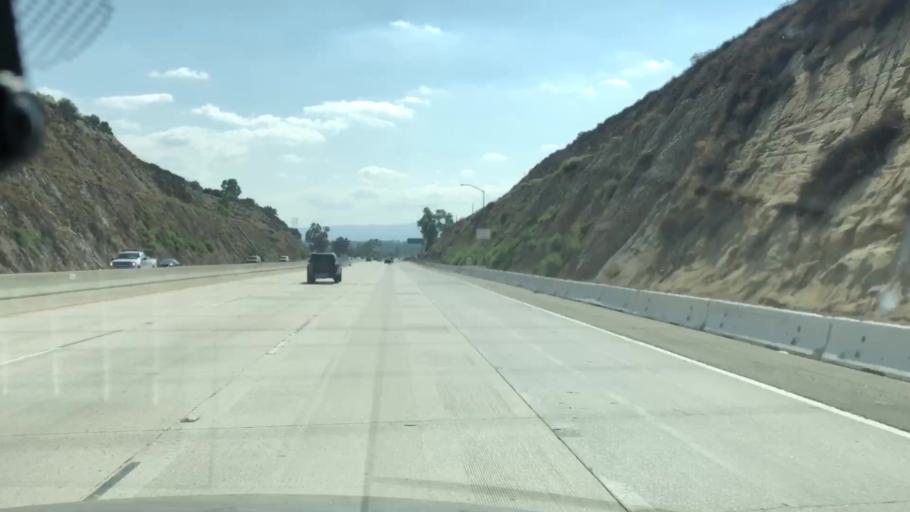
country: US
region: California
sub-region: Los Angeles County
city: San Fernando
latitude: 34.2855
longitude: -118.4682
